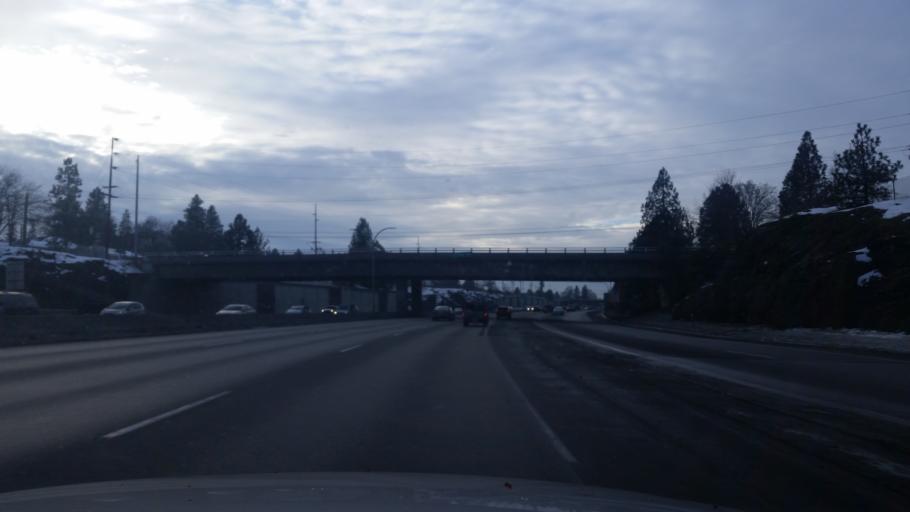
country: US
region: Washington
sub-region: Spokane County
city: Spokane
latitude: 47.6524
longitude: -117.3941
